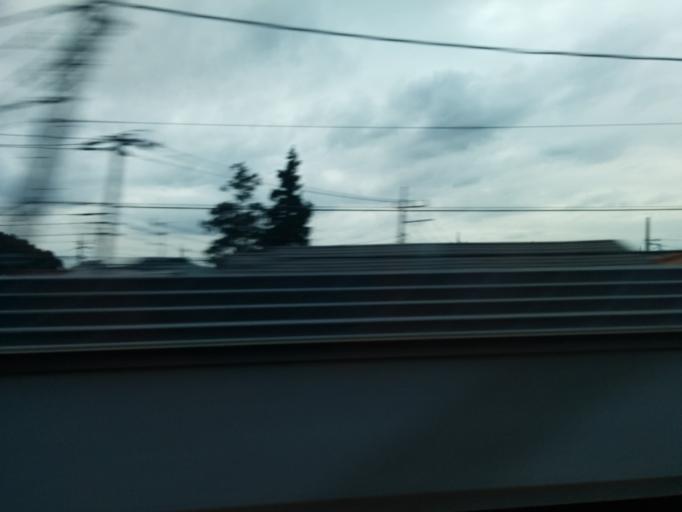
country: JP
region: Kanagawa
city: Yokohama
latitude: 35.4683
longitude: 139.5481
